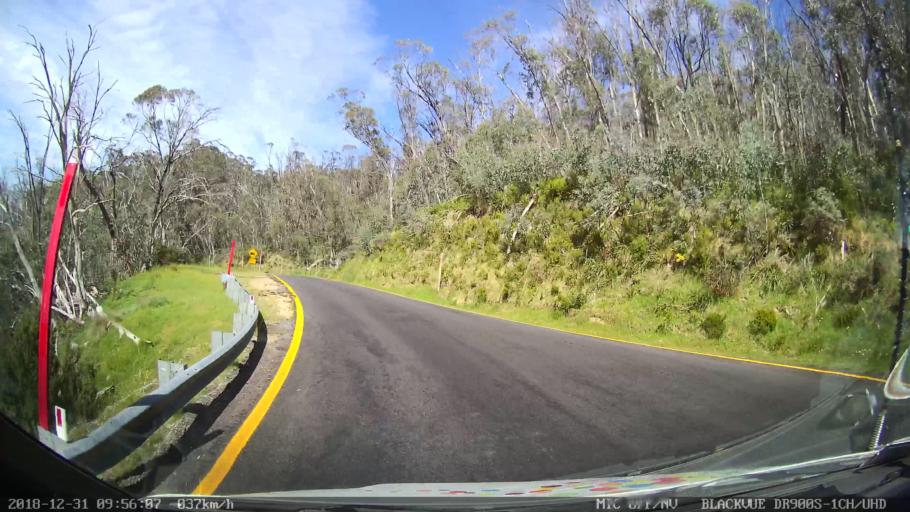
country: AU
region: New South Wales
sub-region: Snowy River
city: Jindabyne
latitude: -36.5301
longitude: 148.2259
